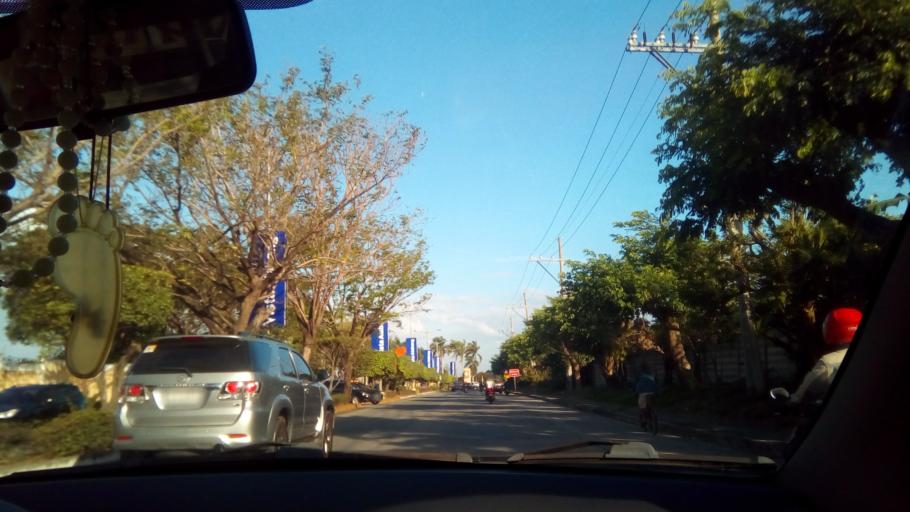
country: PH
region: Calabarzon
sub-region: Province of Laguna
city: San Pedro
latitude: 14.3832
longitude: 121.0117
